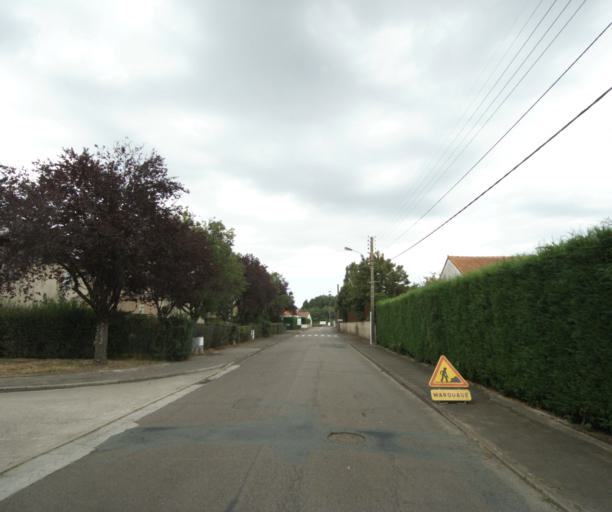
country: FR
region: Bourgogne
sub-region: Departement de Saone-et-Loire
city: Gueugnon
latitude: 46.6067
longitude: 4.0616
